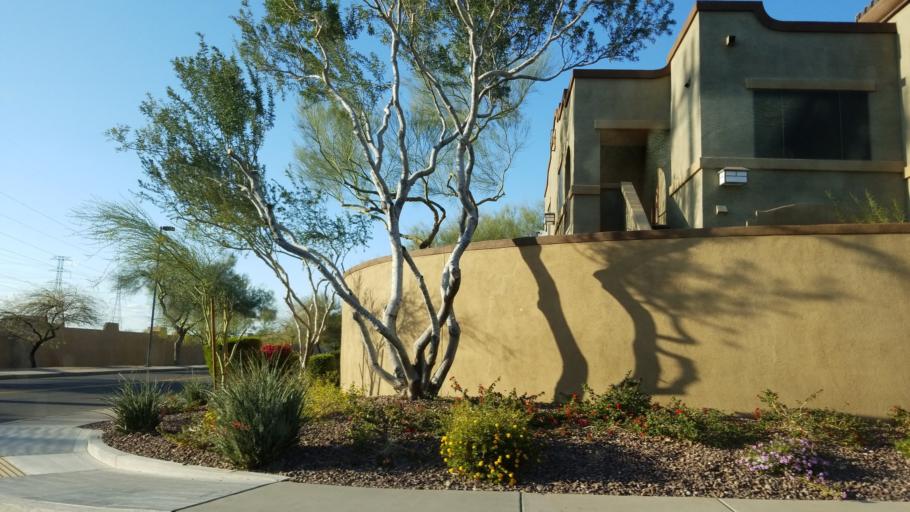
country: US
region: Arizona
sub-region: Maricopa County
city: Scottsdale
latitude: 33.5848
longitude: -111.8313
